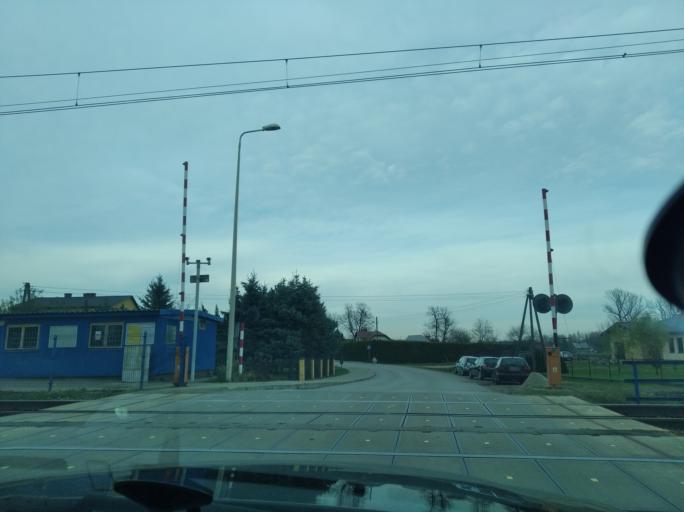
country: PL
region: Subcarpathian Voivodeship
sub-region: Powiat przeworski
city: Grzeska
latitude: 50.0797
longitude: 22.4544
